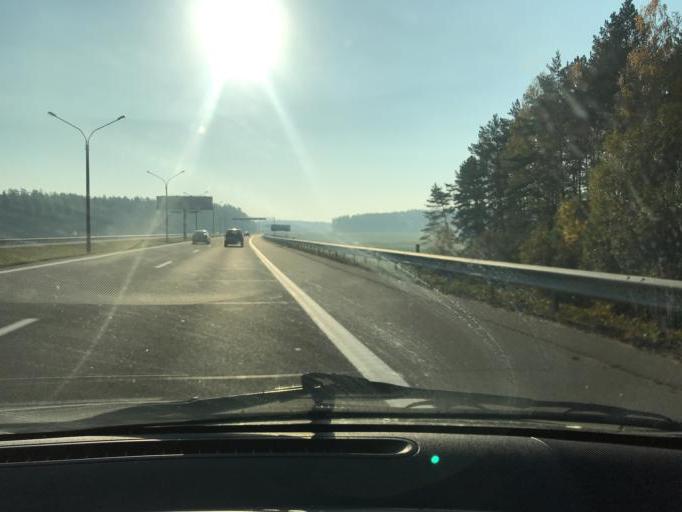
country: BY
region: Minsk
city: Slabada
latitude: 53.9582
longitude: 27.9673
